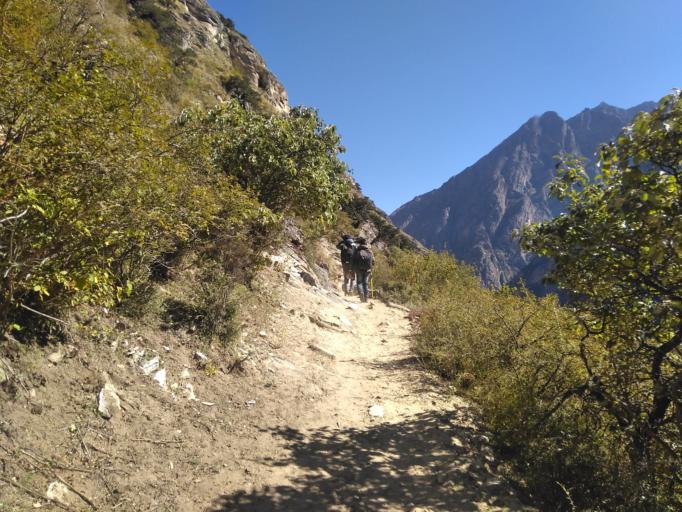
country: NP
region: Western Region
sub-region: Dhawalagiri Zone
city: Jomsom
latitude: 28.9356
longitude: 83.0501
